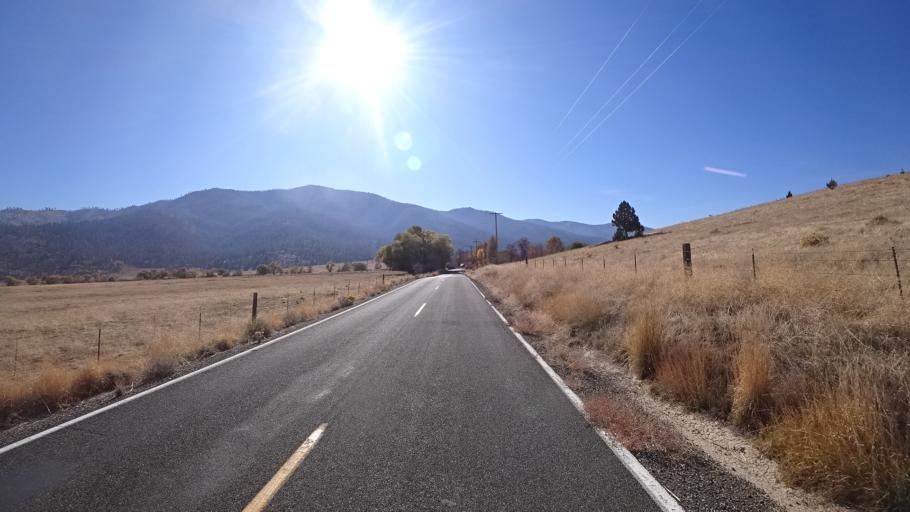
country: US
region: California
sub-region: Siskiyou County
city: Weed
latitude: 41.4963
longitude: -122.5512
